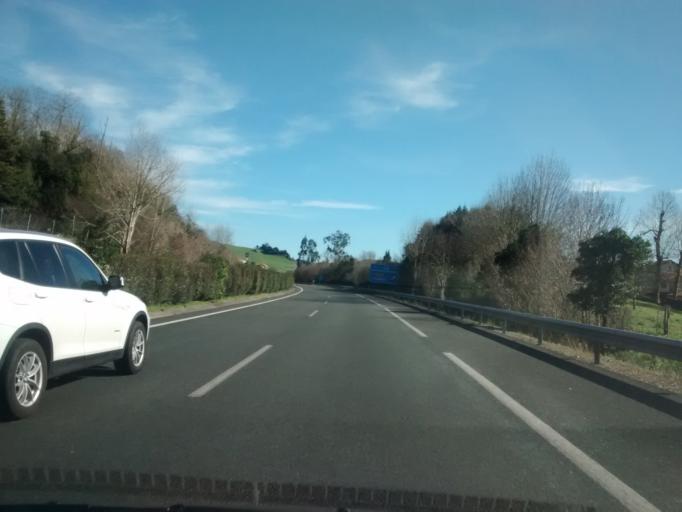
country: ES
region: Cantabria
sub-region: Provincia de Cantabria
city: Entrambasaguas
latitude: 43.3911
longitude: -3.6955
